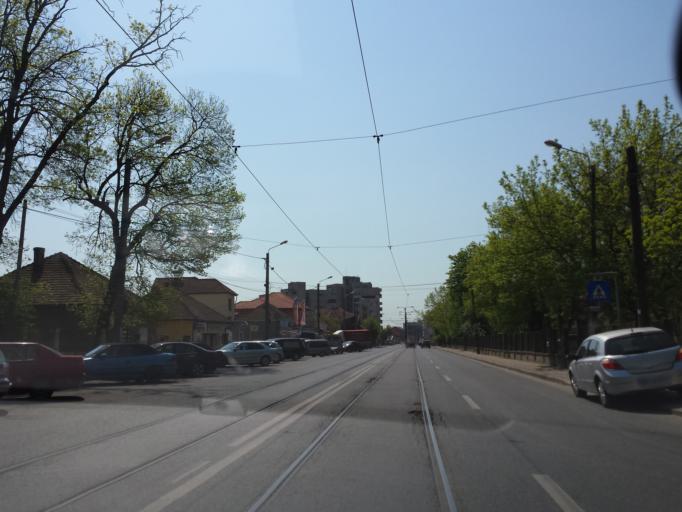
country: RO
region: Timis
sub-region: Comuna Dumbravita
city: Dumbravita
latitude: 45.7688
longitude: 21.2604
